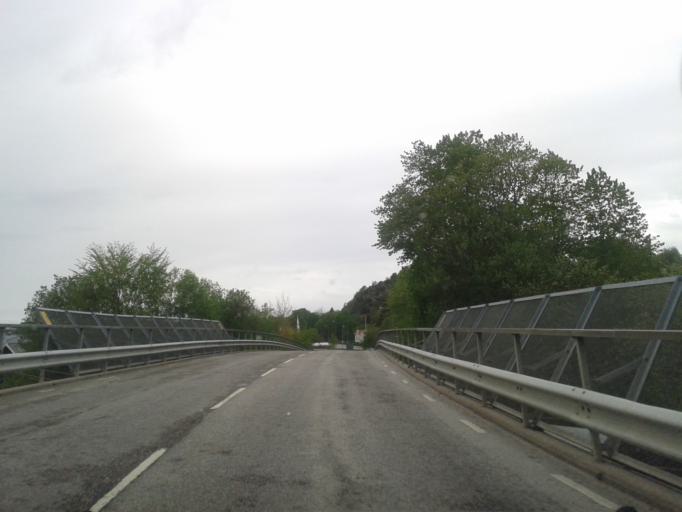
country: SE
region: Vaestra Goetaland
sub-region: Stenungsunds Kommun
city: Stora Hoga
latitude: 58.0176
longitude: 11.8355
